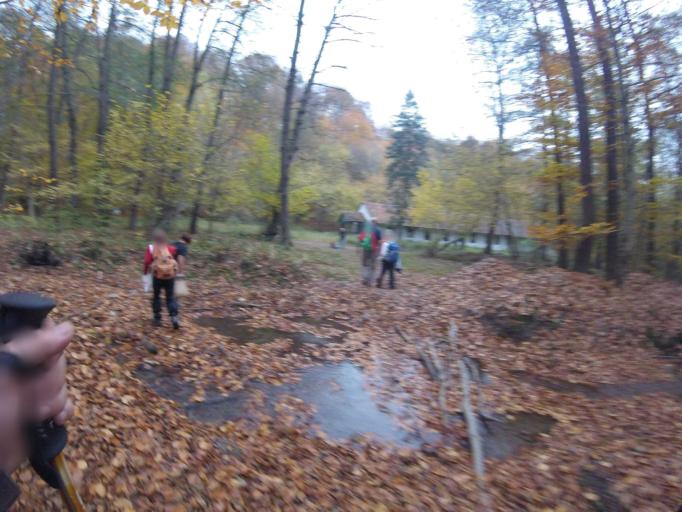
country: HU
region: Borsod-Abauj-Zemplen
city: Tolcsva
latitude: 48.4222
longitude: 21.4234
